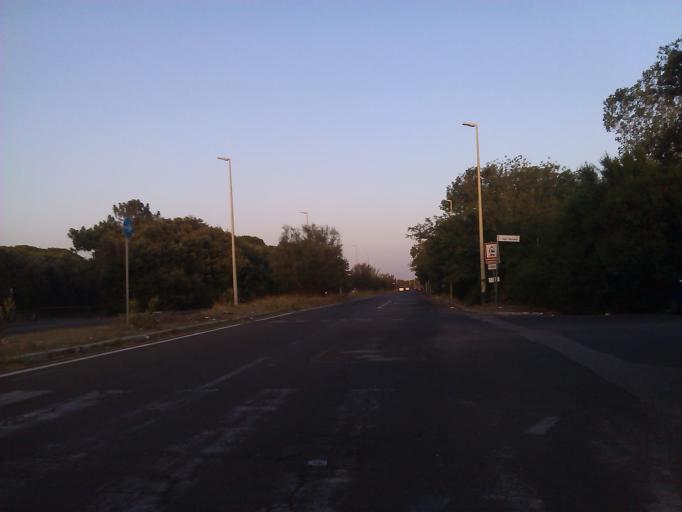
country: IT
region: Latium
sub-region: Citta metropolitana di Roma Capitale
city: Acilia-Castel Fusano-Ostia Antica
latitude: 41.7072
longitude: 12.3381
